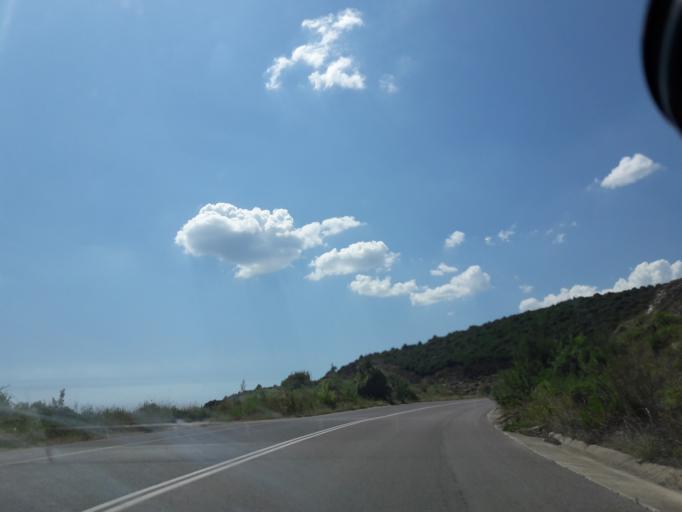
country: GR
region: Central Macedonia
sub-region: Nomos Chalkidikis
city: Ormylia
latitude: 40.3710
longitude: 23.6083
